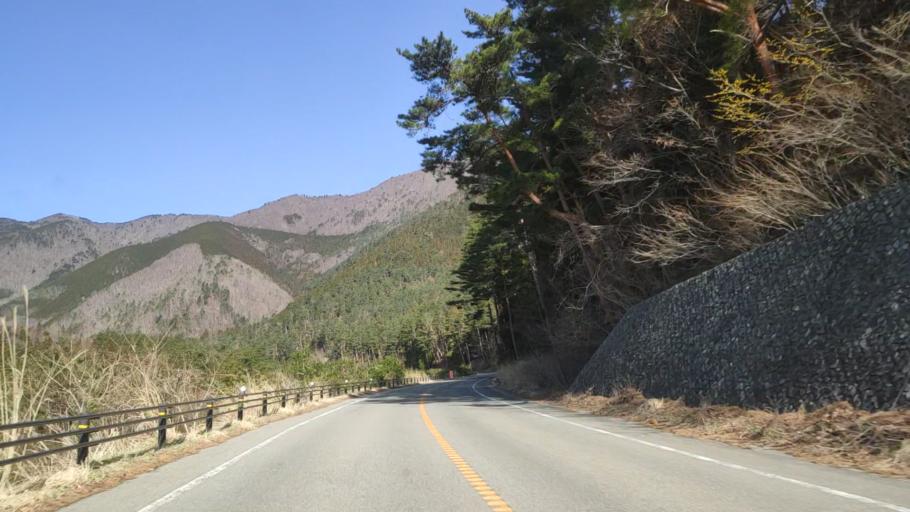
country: JP
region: Yamanashi
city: Fujikawaguchiko
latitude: 35.5260
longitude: 138.7197
